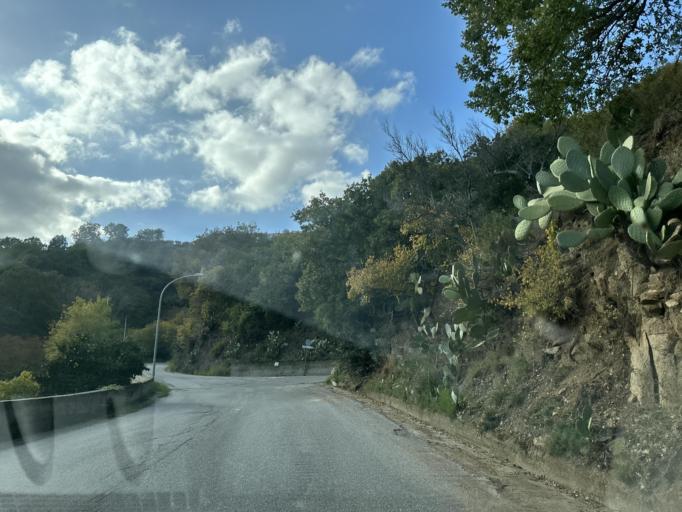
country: IT
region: Calabria
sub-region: Provincia di Catanzaro
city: Montepaone
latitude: 38.7226
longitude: 16.5040
